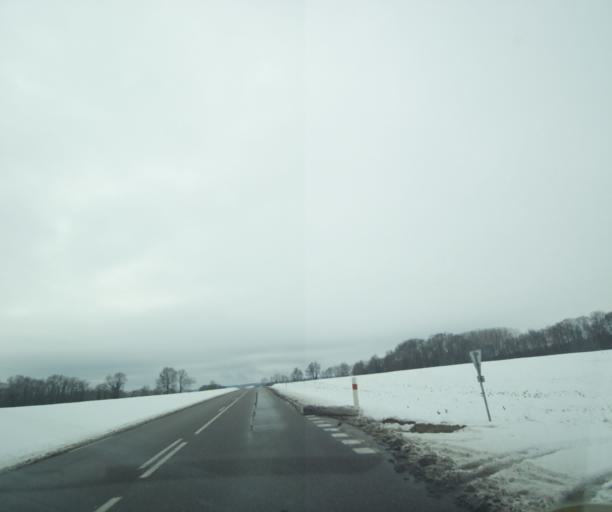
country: FR
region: Champagne-Ardenne
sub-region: Departement de la Haute-Marne
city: Montier-en-Der
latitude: 48.4545
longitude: 4.7446
